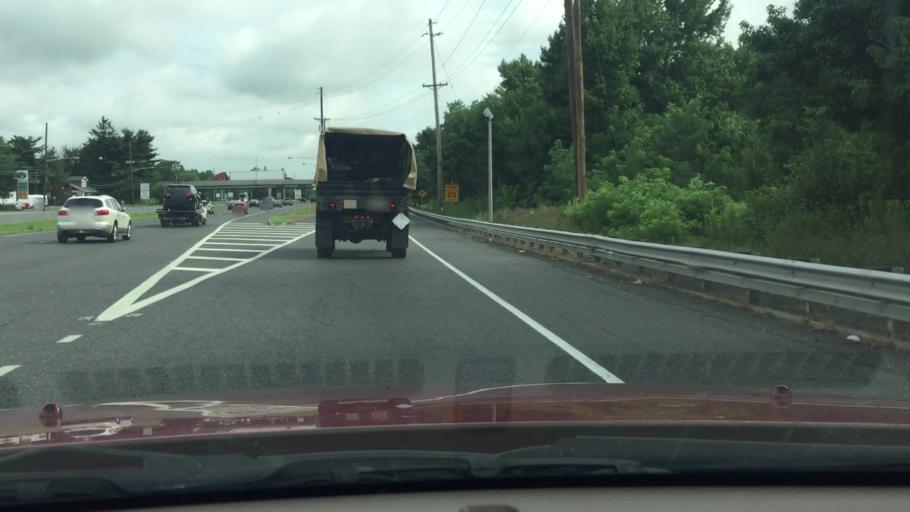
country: US
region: New Jersey
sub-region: Burlington County
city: Bordentown
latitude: 40.1214
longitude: -74.7065
